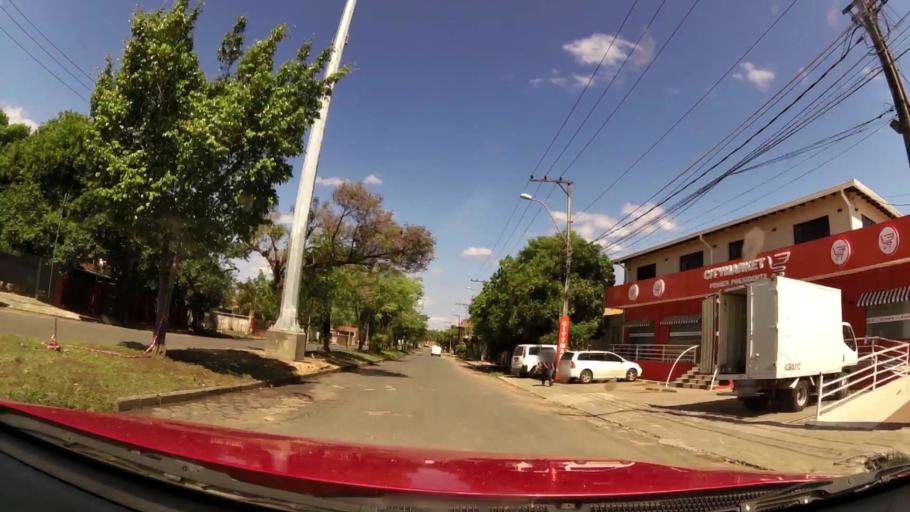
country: PY
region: Central
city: Fernando de la Mora
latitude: -25.2684
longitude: -57.5490
